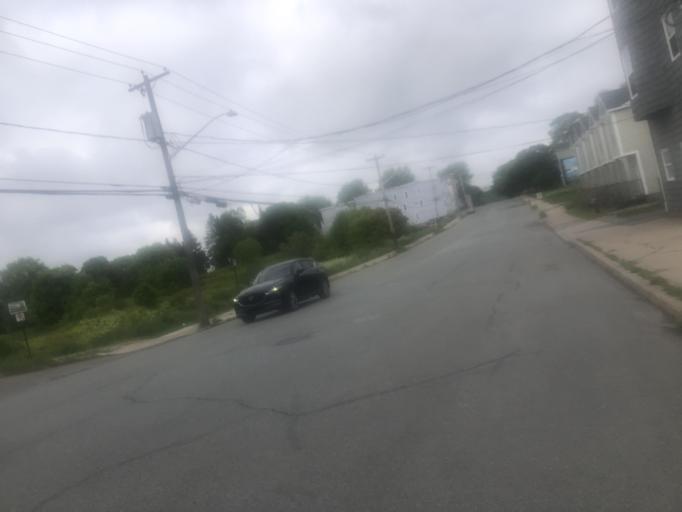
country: CA
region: New Brunswick
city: Saint John
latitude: 45.2756
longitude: -66.0832
